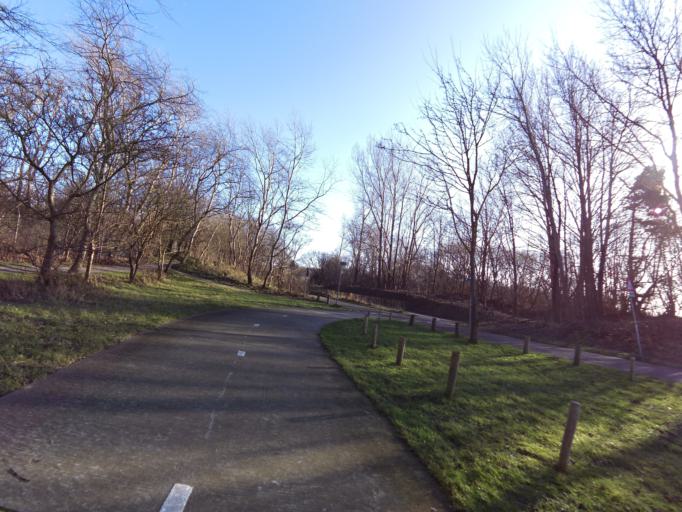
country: NL
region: South Holland
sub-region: Gemeente Hellevoetsluis
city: Nieuw-Helvoet
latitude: 51.8767
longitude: 4.0486
